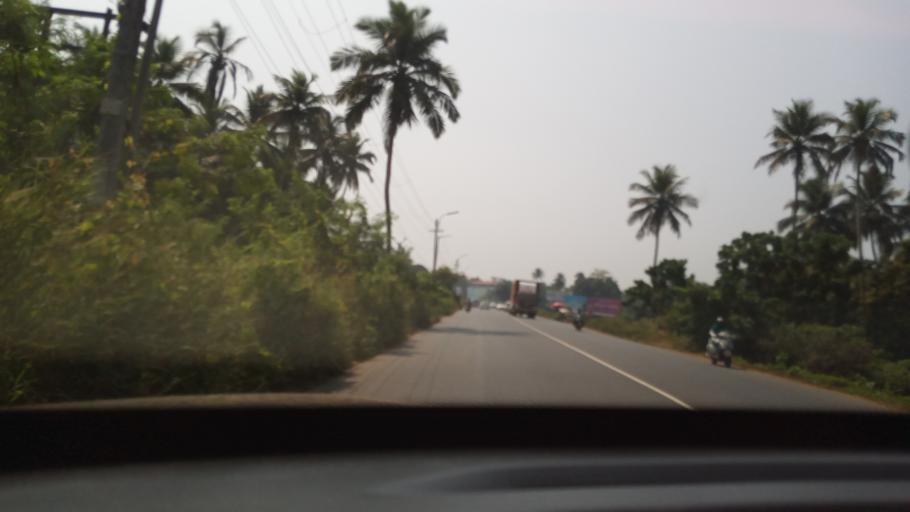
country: IN
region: Goa
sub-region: South Goa
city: Sancoale
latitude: 15.3371
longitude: 73.9276
